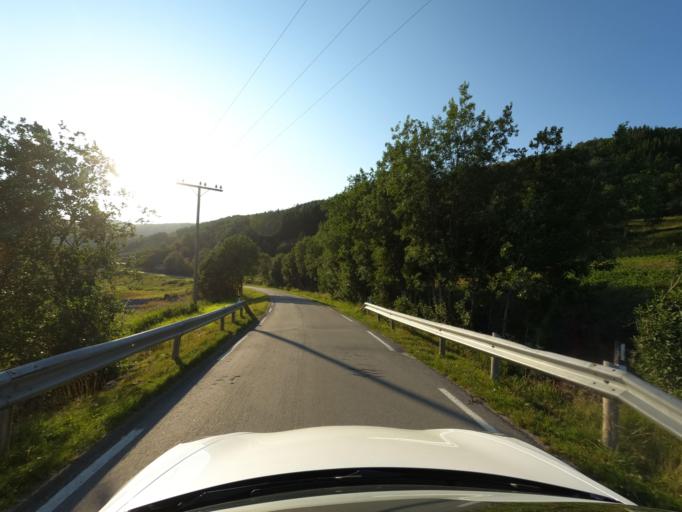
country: NO
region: Nordland
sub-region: Ballangen
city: Ballangen
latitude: 68.4680
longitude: 16.8111
